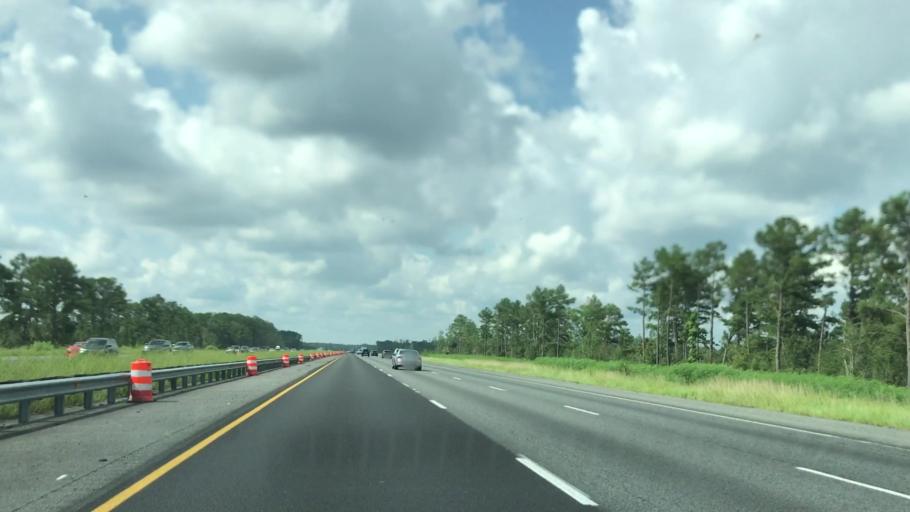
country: US
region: Georgia
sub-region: Camden County
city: Woodbine
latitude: 31.0076
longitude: -81.6615
